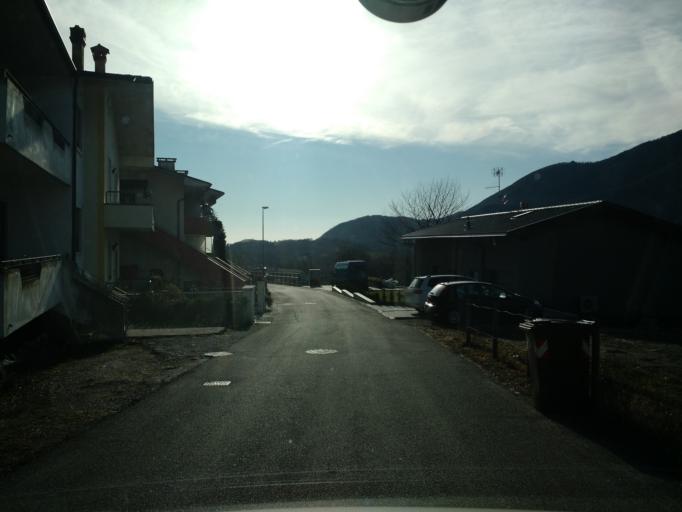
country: IT
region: Veneto
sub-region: Provincia di Vicenza
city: Cogollo del Cengio
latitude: 45.7952
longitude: 11.3997
